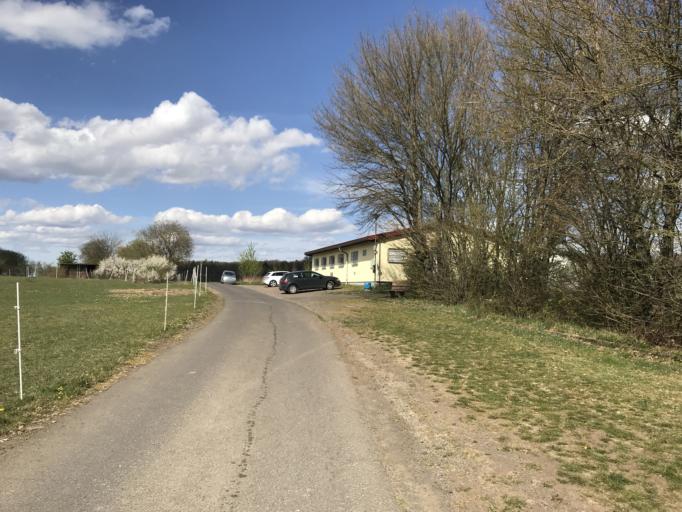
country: DE
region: Hesse
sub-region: Regierungsbezirk Giessen
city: Rabenau
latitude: 50.6962
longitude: 8.8375
